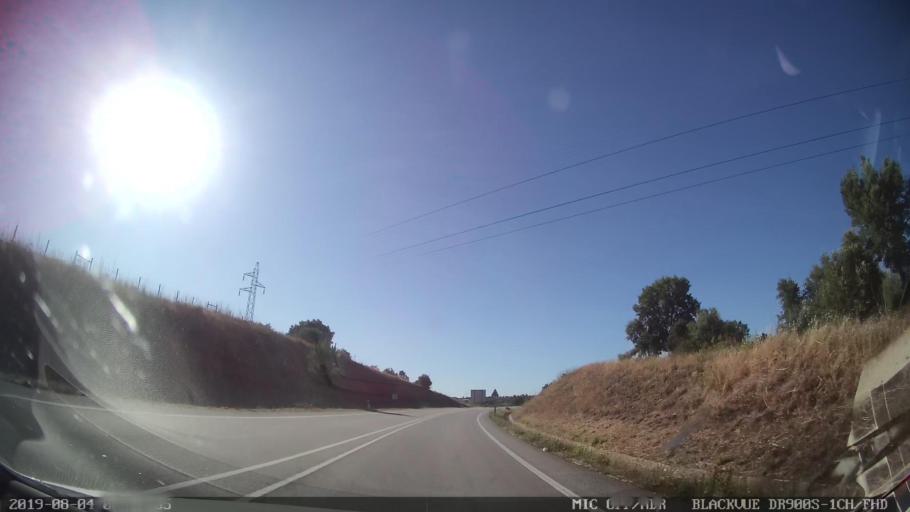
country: PT
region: Santarem
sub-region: Abrantes
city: Alferrarede
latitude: 39.4872
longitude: -8.0977
